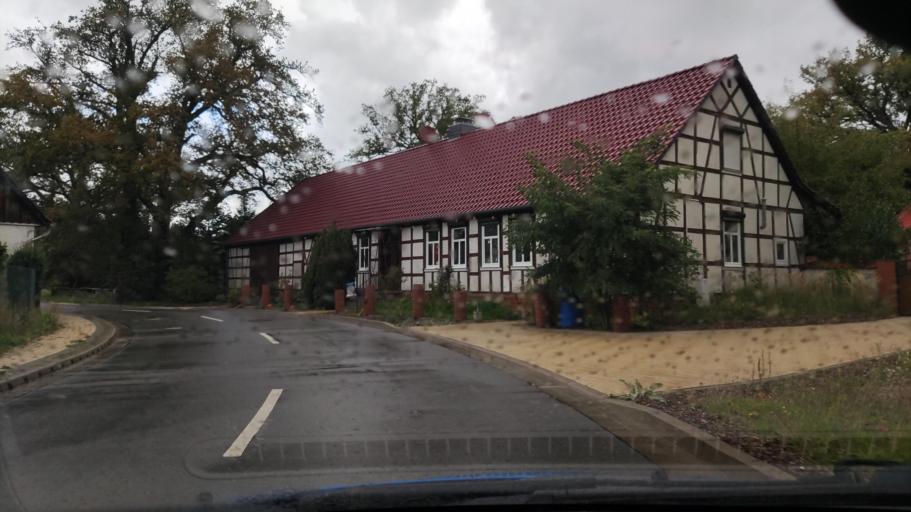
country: DE
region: Lower Saxony
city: Gartow
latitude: 52.9891
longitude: 11.5472
